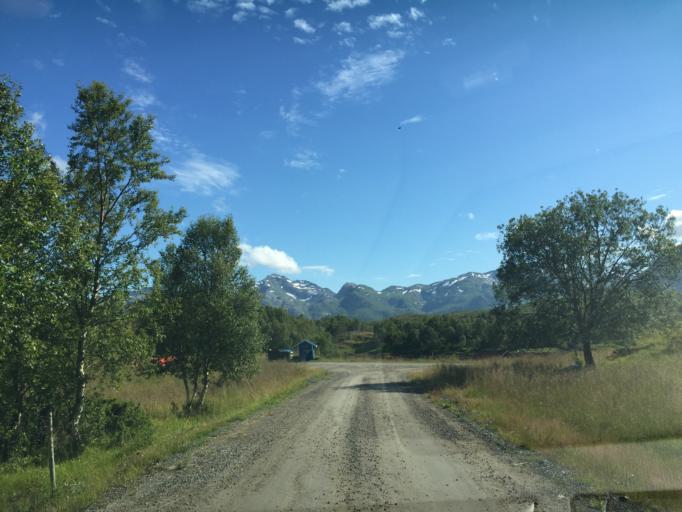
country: NO
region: Nordland
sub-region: Vagan
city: Kabelvag
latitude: 68.3513
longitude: 14.4526
